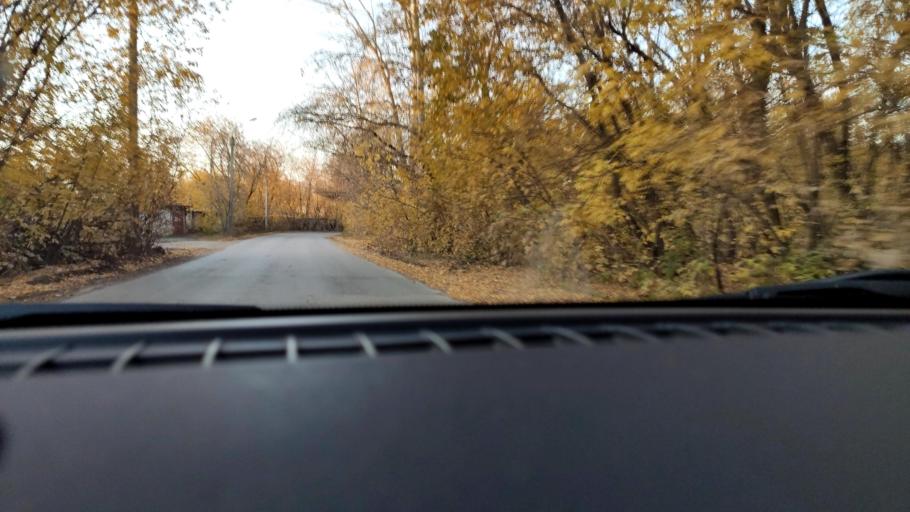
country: RU
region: Perm
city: Perm
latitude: 57.9699
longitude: 56.2764
